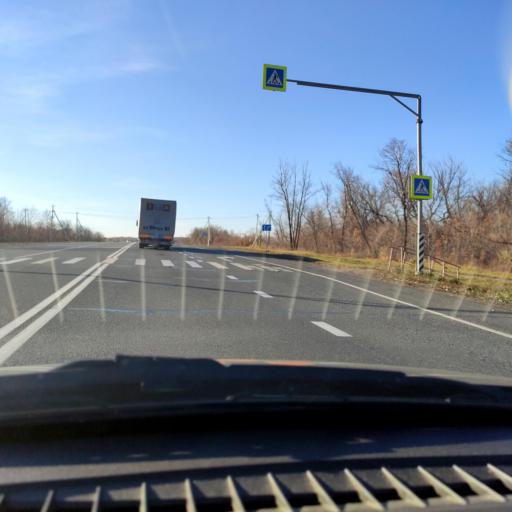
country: RU
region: Samara
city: Mezhdurechensk
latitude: 53.2561
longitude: 49.1316
